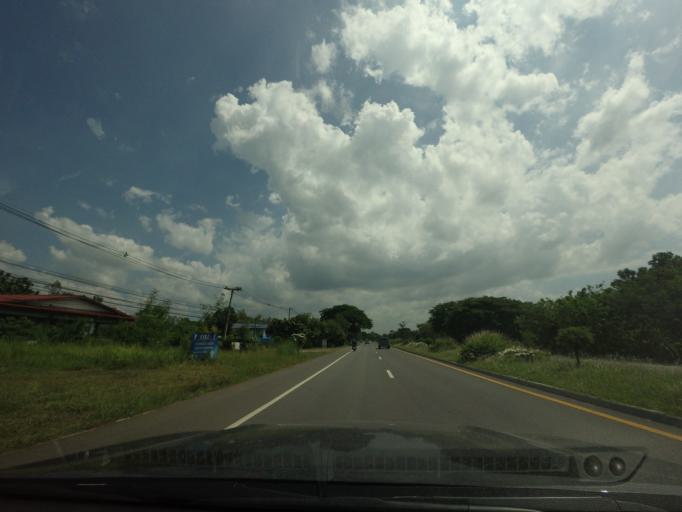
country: TH
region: Phetchabun
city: Phetchabun
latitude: 16.2287
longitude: 101.0865
